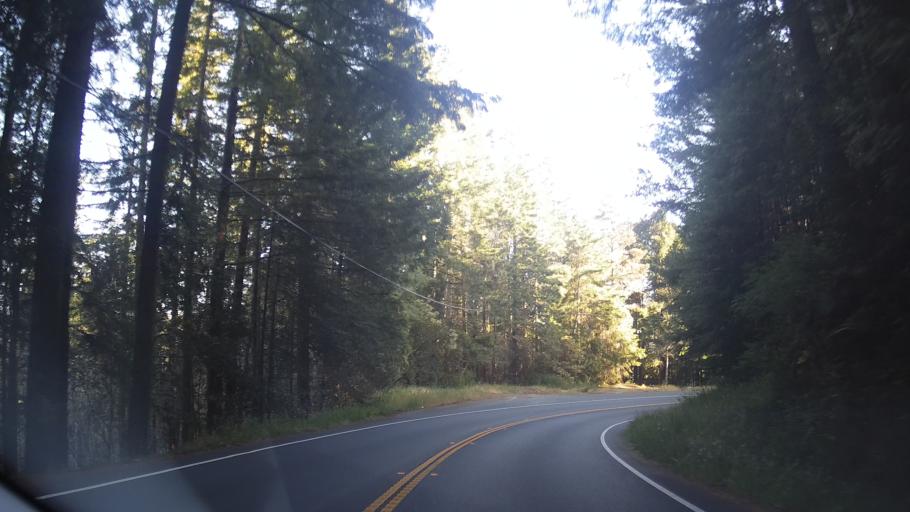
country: US
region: California
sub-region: Mendocino County
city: Fort Bragg
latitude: 39.4043
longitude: -123.7355
